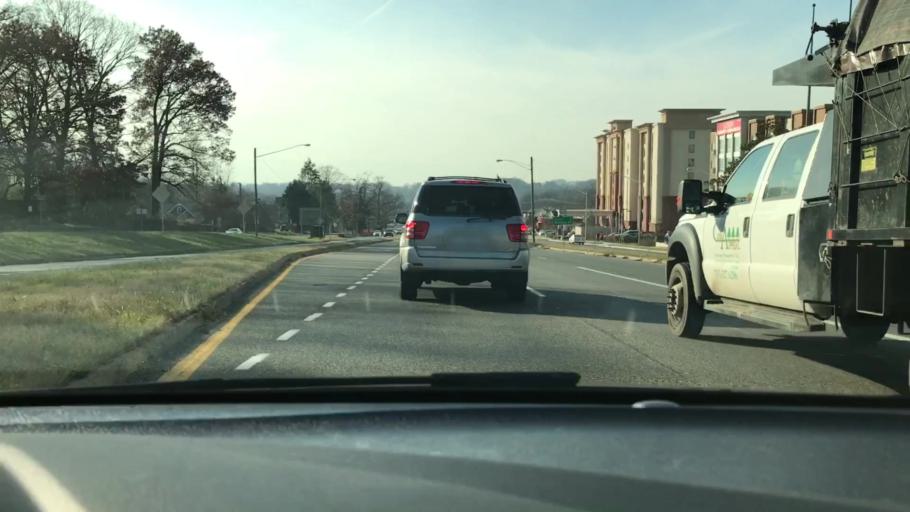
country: US
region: Virginia
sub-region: Fairfax County
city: Seven Corners
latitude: 38.8723
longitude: -77.1597
